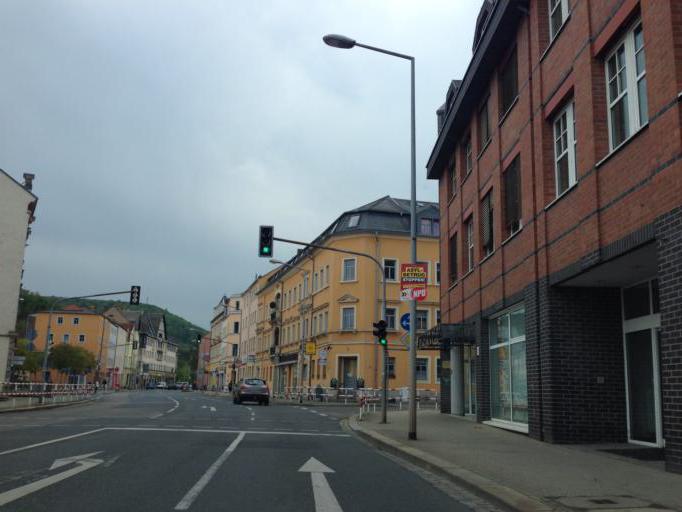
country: DE
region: Saxony
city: Freital
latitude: 51.0123
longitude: 13.6622
